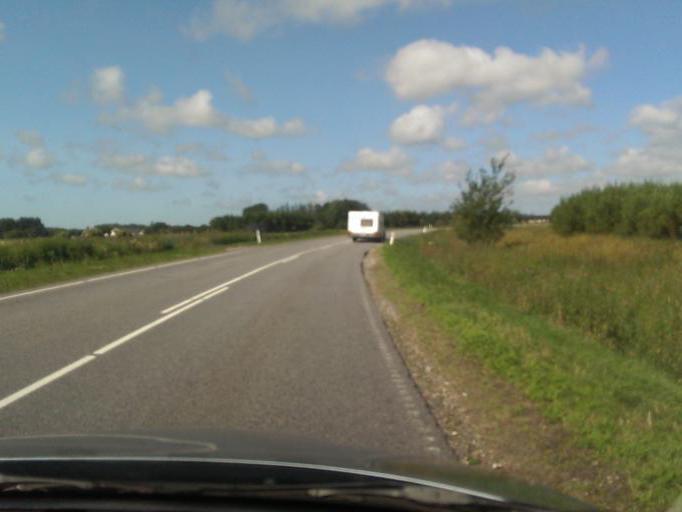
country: DK
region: North Denmark
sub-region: Alborg Kommune
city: Vadum
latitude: 57.2053
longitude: 9.8720
